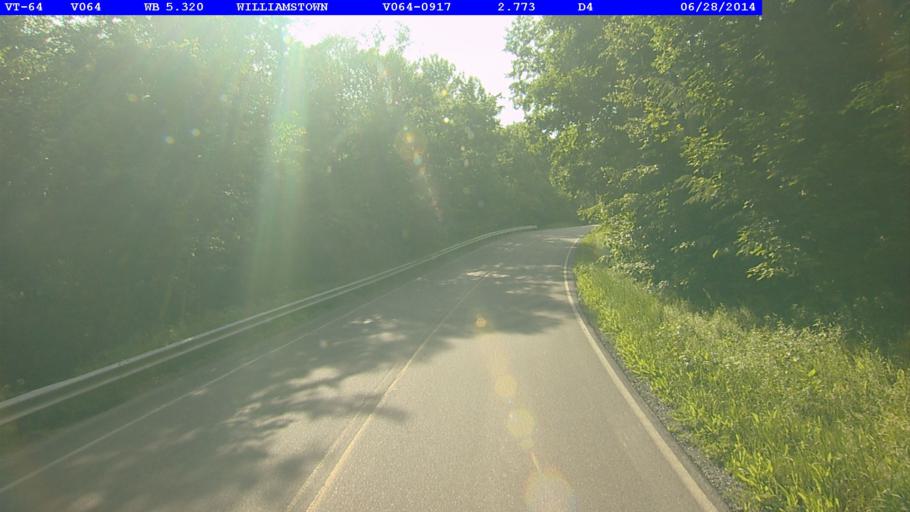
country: US
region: Vermont
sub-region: Orange County
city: Williamstown
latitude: 44.1154
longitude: -72.5664
